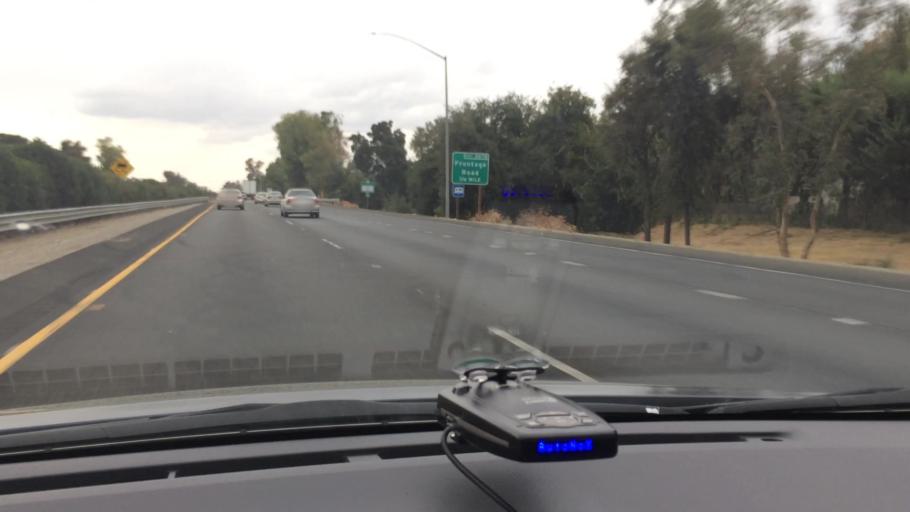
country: US
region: California
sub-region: San Joaquin County
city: Lodi
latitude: 38.1465
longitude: -121.2612
